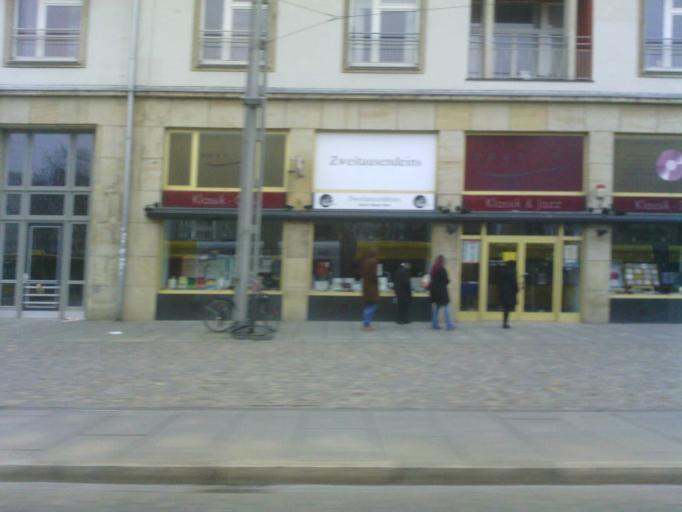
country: DE
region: Saxony
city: Dresden
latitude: 51.0497
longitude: 13.7338
